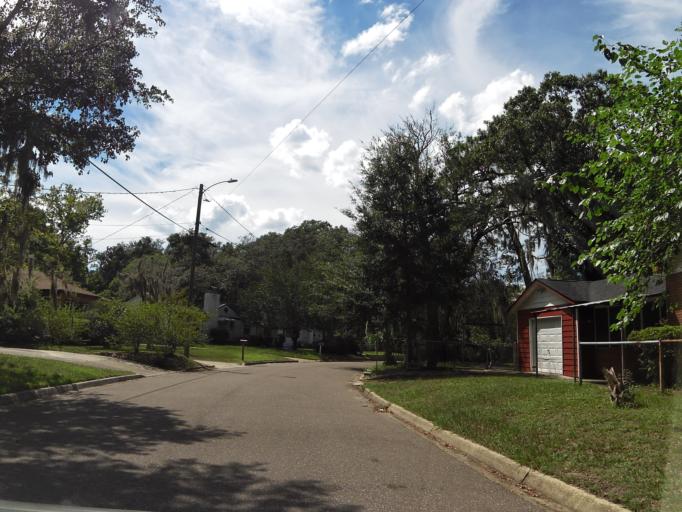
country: US
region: Florida
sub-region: Duval County
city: Jacksonville
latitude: 30.3830
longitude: -81.6451
